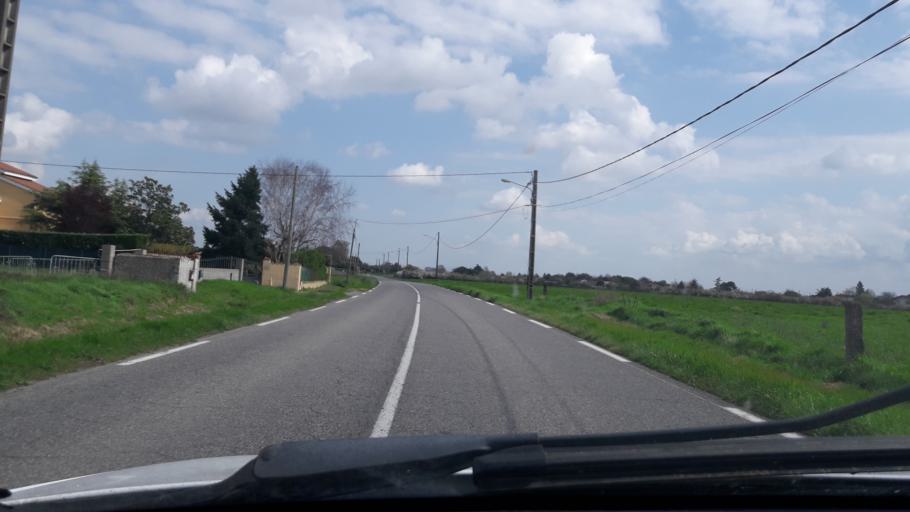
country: FR
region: Midi-Pyrenees
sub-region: Departement de la Haute-Garonne
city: Seysses
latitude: 43.5001
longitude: 1.2855
